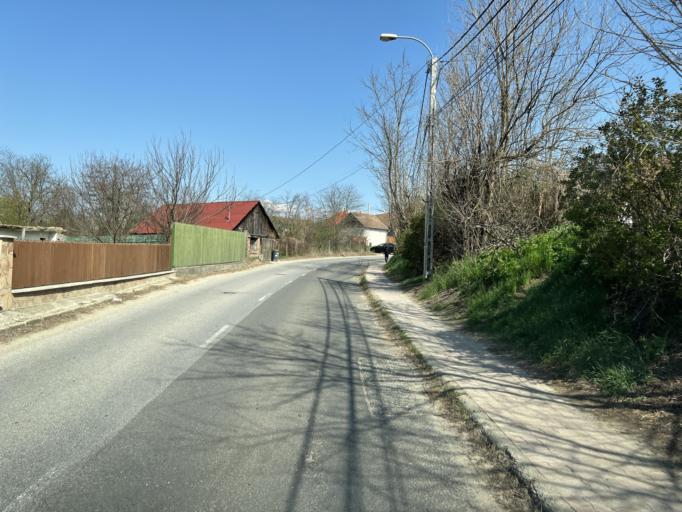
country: HU
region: Pest
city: Orbottyan
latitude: 47.6919
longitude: 19.2894
